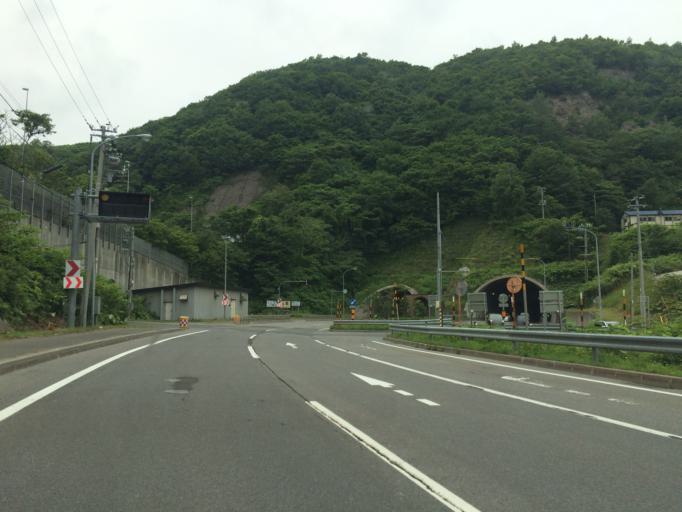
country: JP
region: Hokkaido
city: Otaru
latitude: 43.1621
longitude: 141.1003
